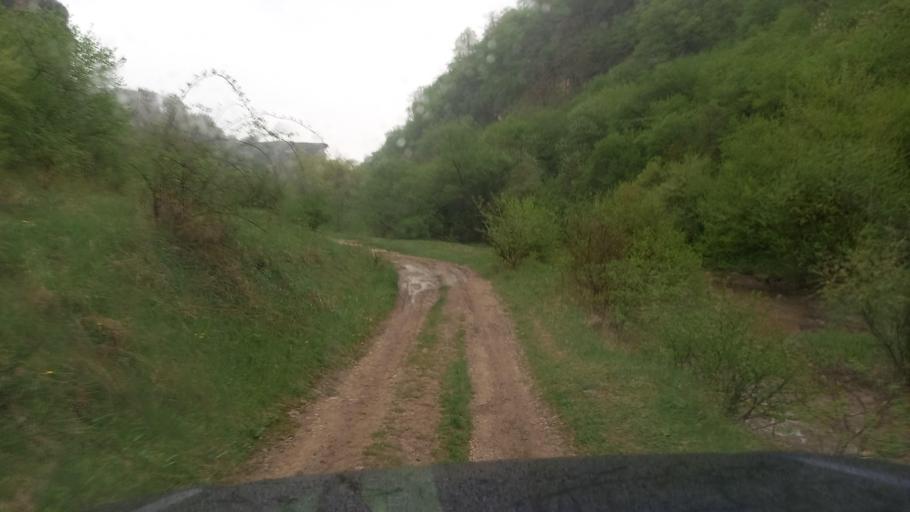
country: RU
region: Stavropol'skiy
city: Kislovodsk
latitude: 43.8842
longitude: 42.6973
